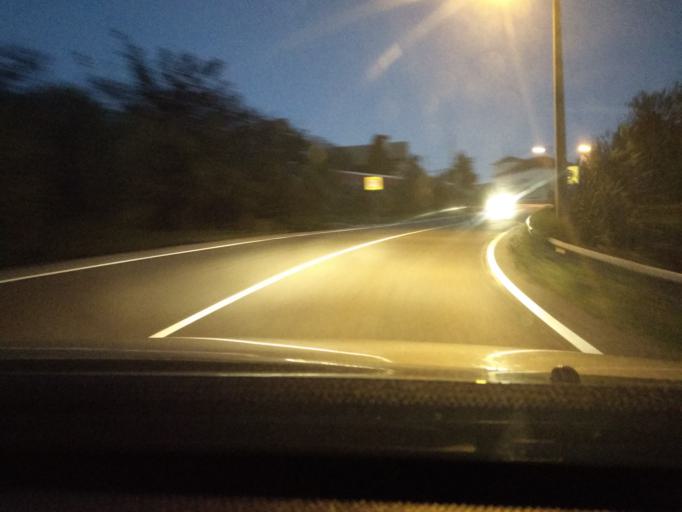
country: ES
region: Galicia
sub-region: Provincia de Pontevedra
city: Moana
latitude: 42.2903
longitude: -8.7440
